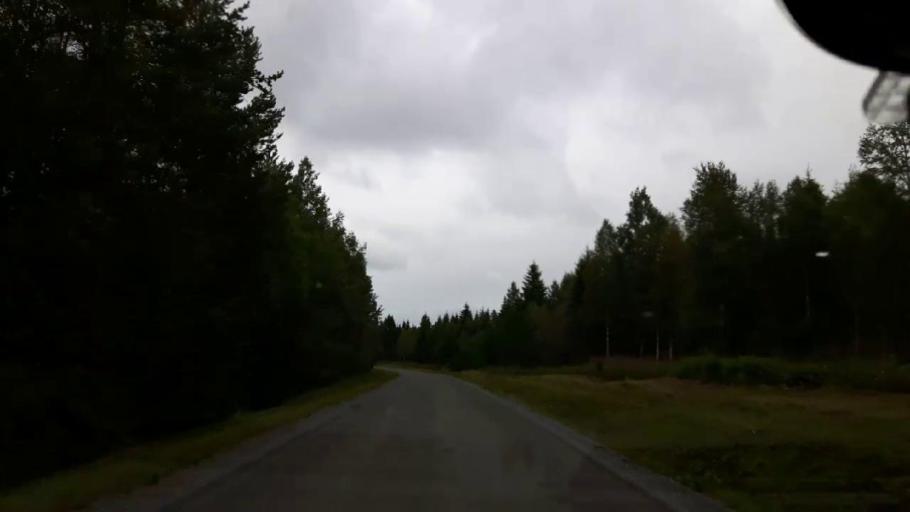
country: SE
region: Jaemtland
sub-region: OEstersunds Kommun
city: Ostersund
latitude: 63.0671
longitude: 14.5526
